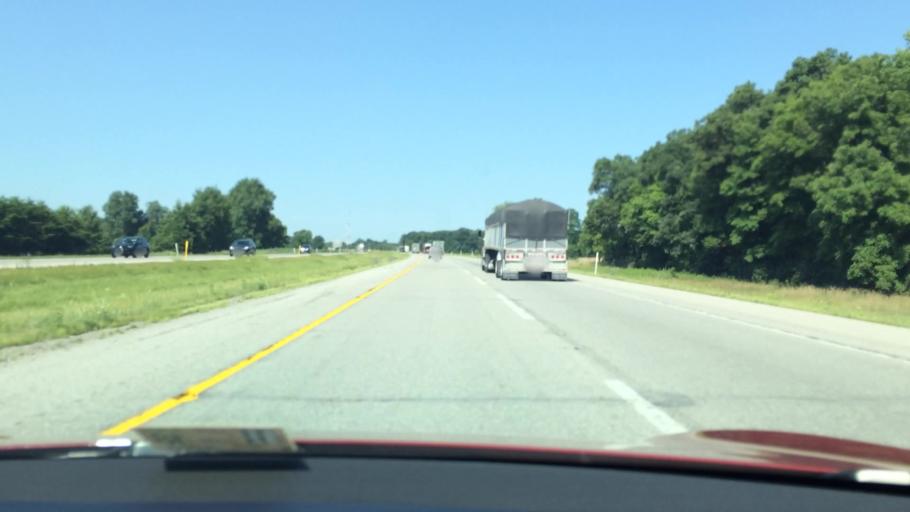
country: US
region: Indiana
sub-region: Elkhart County
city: Middlebury
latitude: 41.7469
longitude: -85.7077
